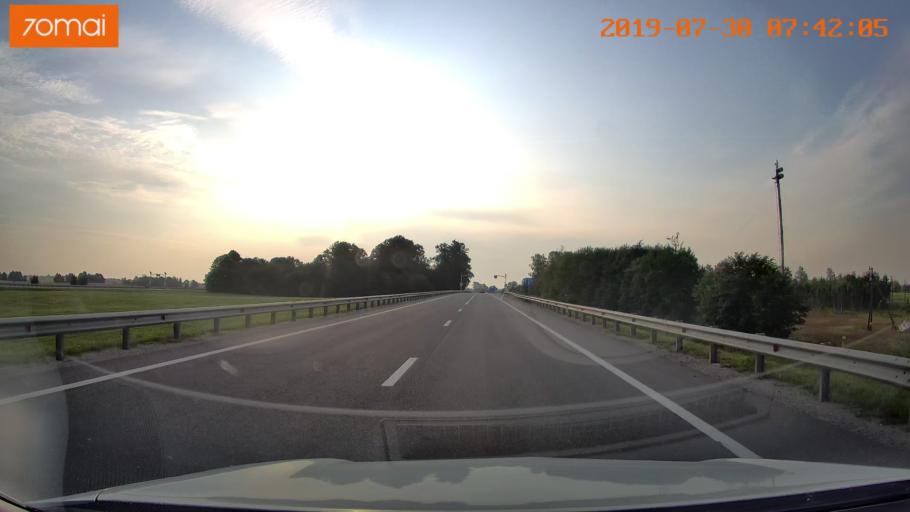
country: RU
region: Kaliningrad
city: Gvardeysk
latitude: 54.6478
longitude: 21.2692
